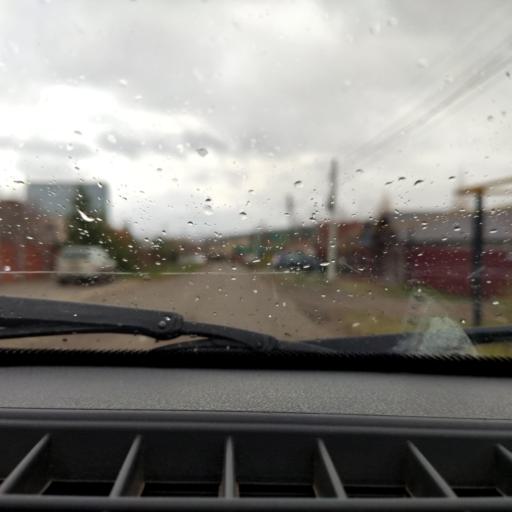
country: RU
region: Bashkortostan
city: Mikhaylovka
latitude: 54.8283
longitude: 55.9048
